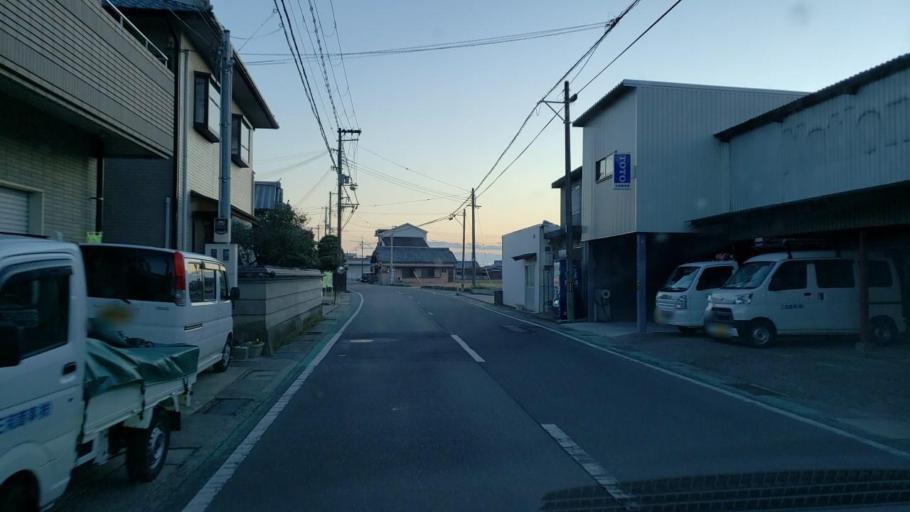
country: JP
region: Hyogo
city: Fukura
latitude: 34.3076
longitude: 134.7645
